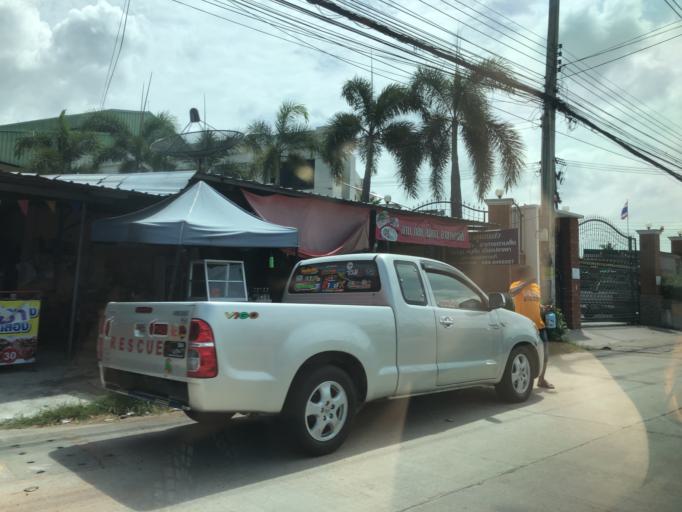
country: TH
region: Chon Buri
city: Si Racha
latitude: 13.1497
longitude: 100.9731
